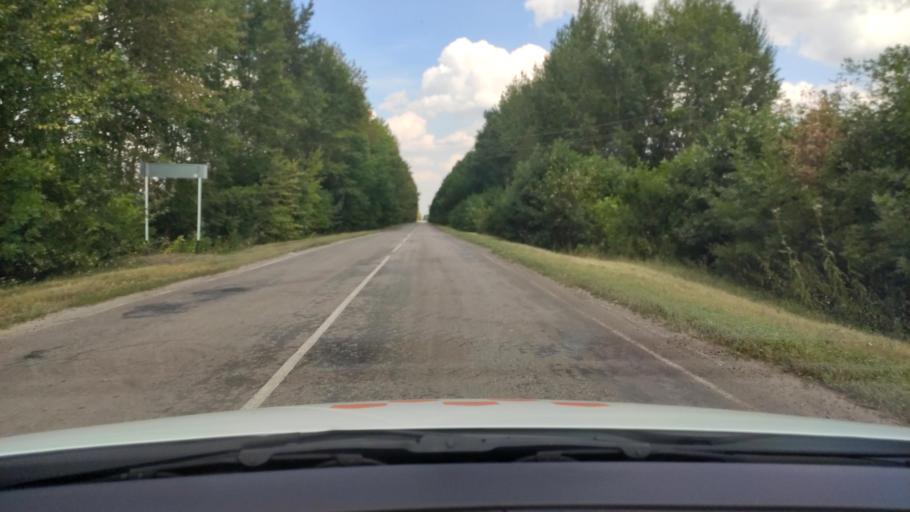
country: RU
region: Voronezj
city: Pereleshinskiy
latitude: 51.7160
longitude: 40.3420
